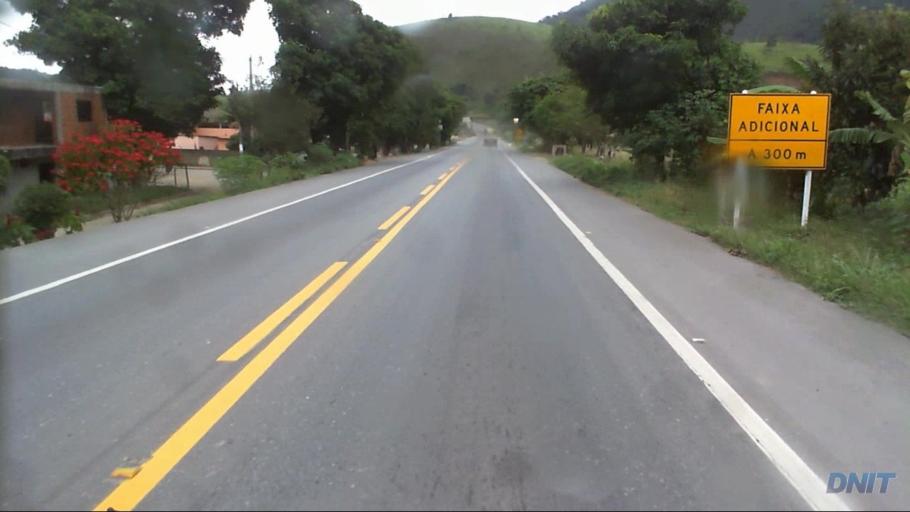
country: BR
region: Minas Gerais
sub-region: Nova Era
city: Nova Era
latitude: -19.7208
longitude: -43.0057
